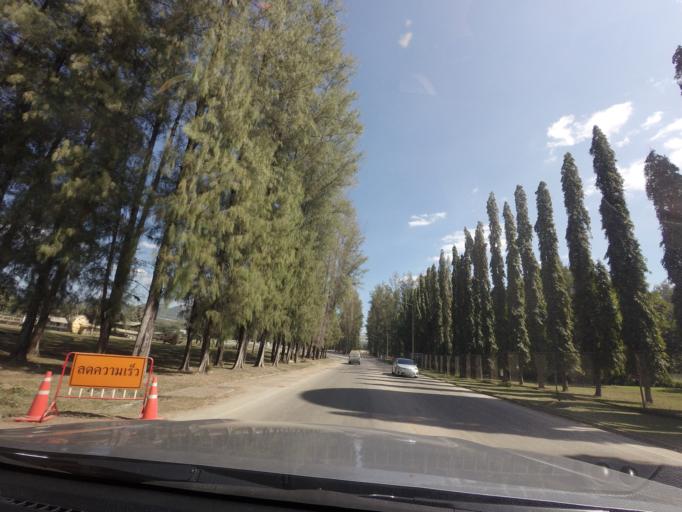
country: TH
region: Lampang
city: Mae Mo
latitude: 18.3043
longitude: 99.7340
